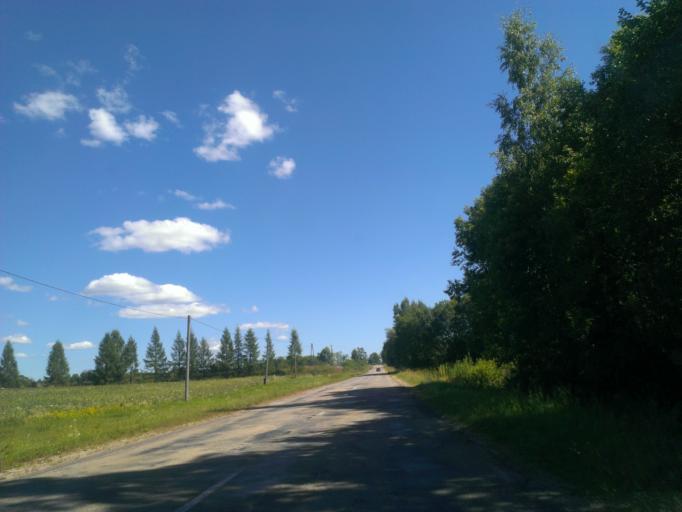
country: LV
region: Malpils
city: Malpils
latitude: 57.0198
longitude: 24.9183
